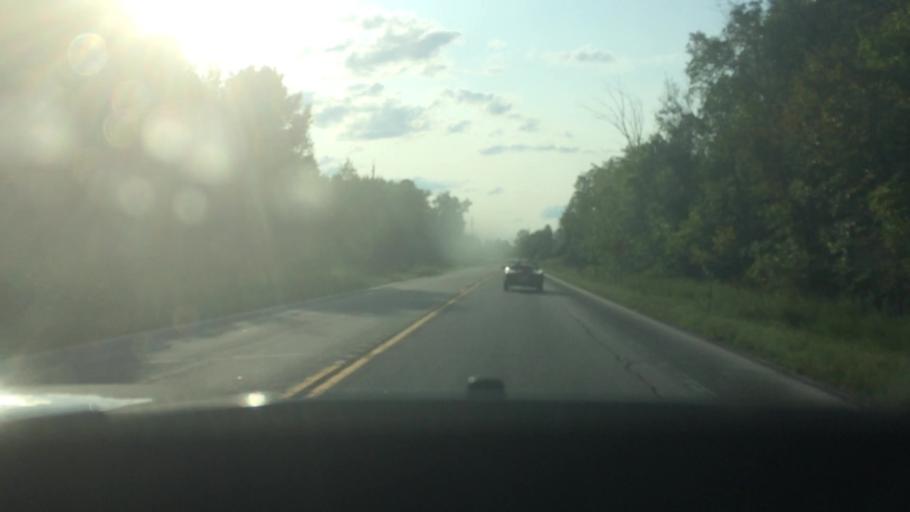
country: US
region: New York
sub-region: St. Lawrence County
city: Canton
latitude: 44.6561
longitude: -75.3176
